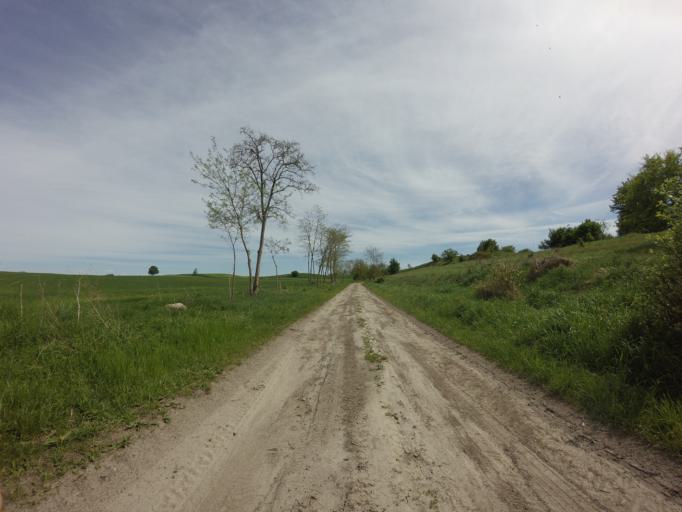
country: PL
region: West Pomeranian Voivodeship
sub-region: Powiat choszczenski
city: Recz
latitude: 53.1745
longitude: 15.5537
